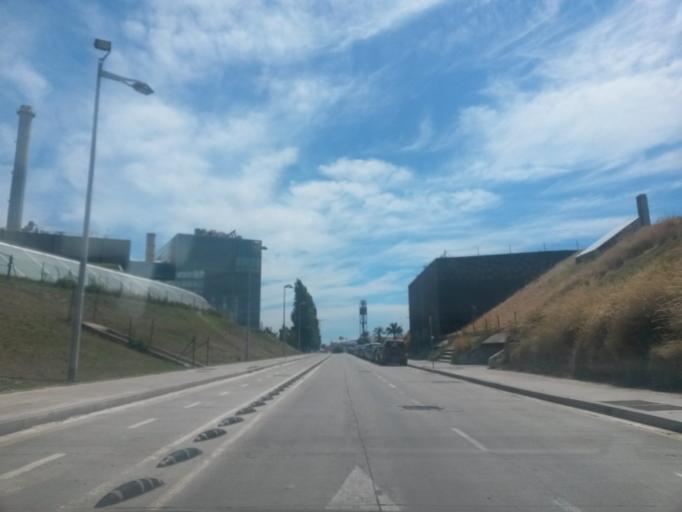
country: ES
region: Catalonia
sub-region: Provincia de Barcelona
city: Sant Adria de Besos
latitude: 41.4182
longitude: 2.2262
